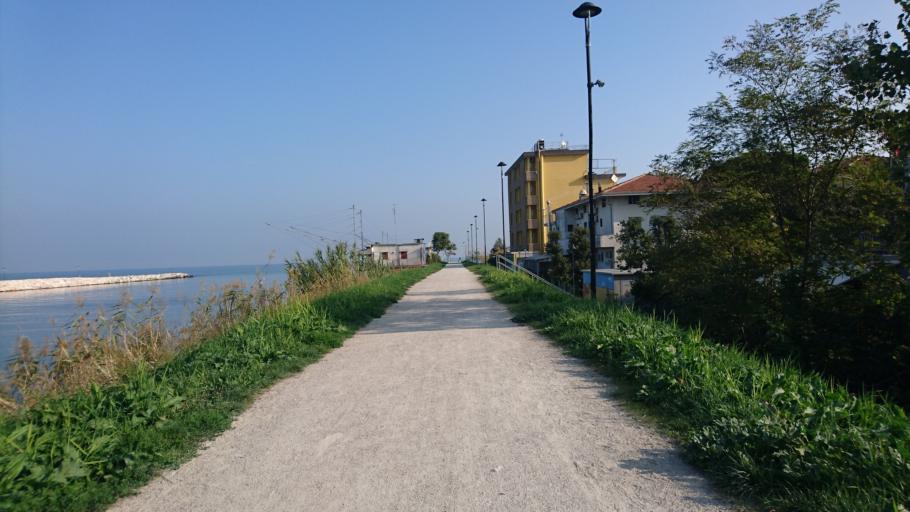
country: IT
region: Emilia-Romagna
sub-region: Provincia di Rimini
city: Rimini
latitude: 44.0742
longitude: 12.5627
